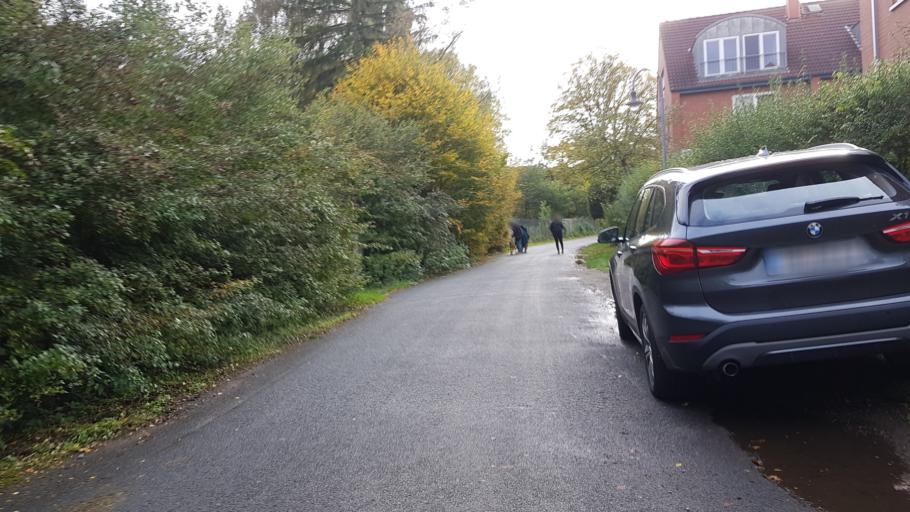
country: DE
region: Bremen
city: Bremen
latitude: 53.0970
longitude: 8.8232
